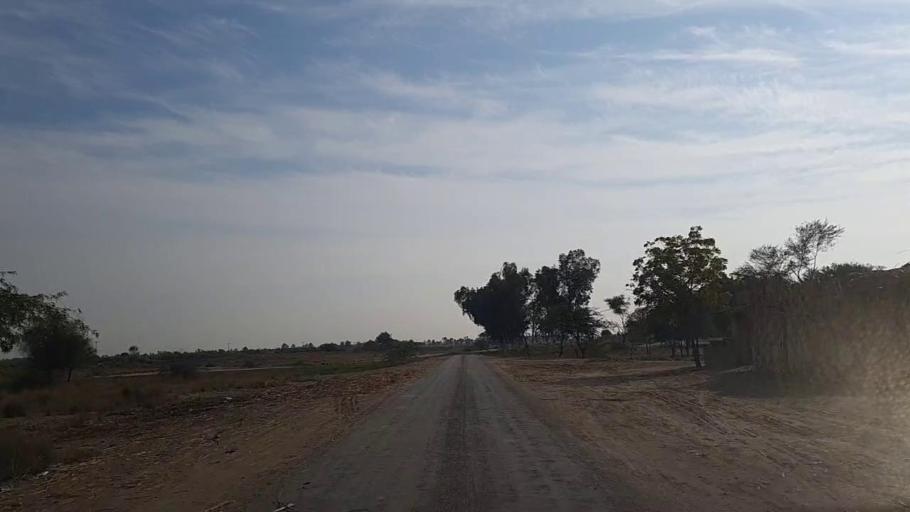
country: PK
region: Sindh
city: Daur
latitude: 26.4718
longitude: 68.4180
